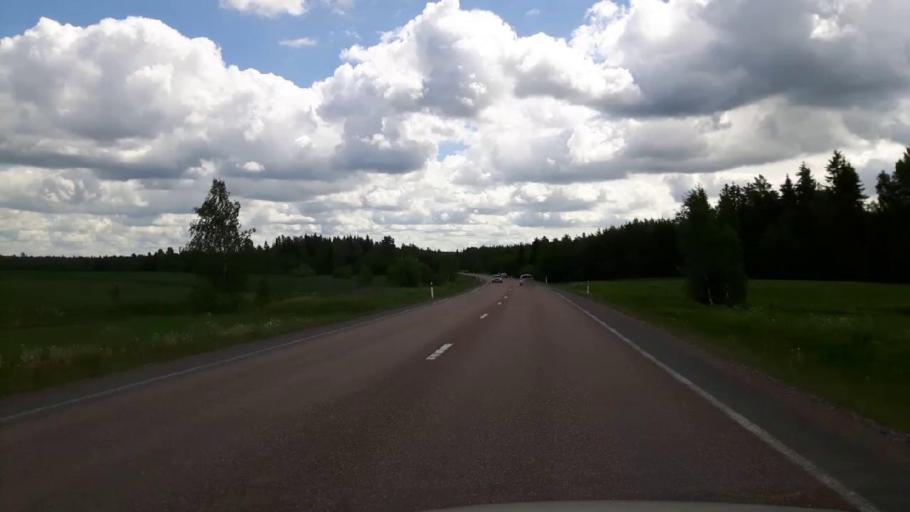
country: SE
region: Dalarna
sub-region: Saters Kommun
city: Saeter
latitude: 60.5011
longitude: 15.7456
